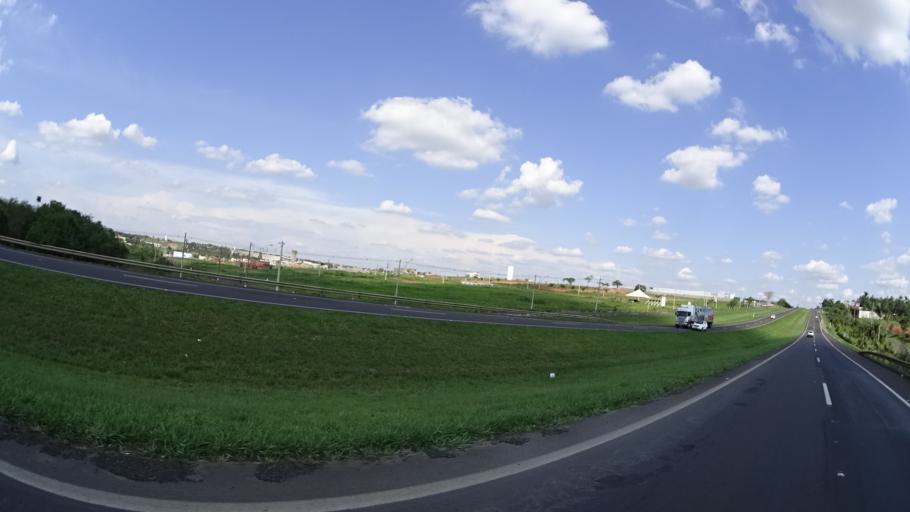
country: BR
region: Sao Paulo
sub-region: Sao Jose Do Rio Preto
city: Sao Jose do Rio Preto
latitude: -20.8604
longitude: -49.3353
